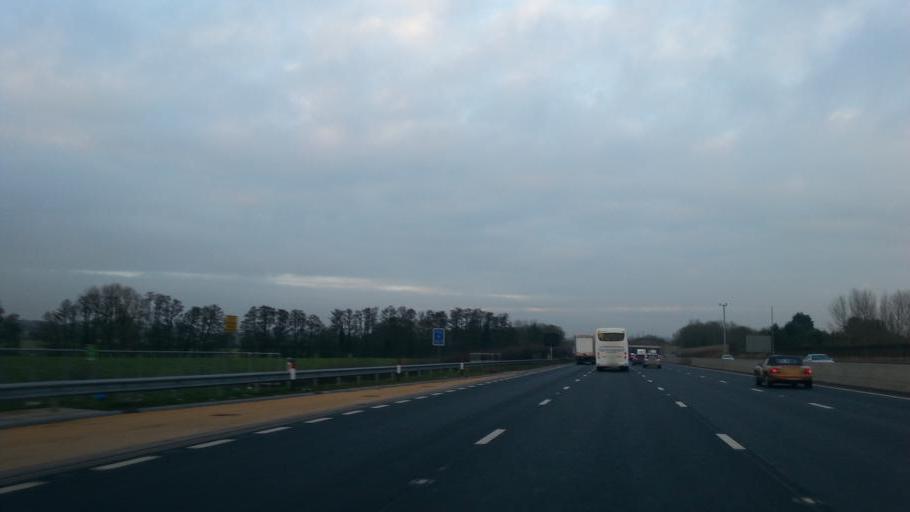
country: GB
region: England
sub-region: Worcestershire
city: Droitwich
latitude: 52.3033
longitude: -2.1103
